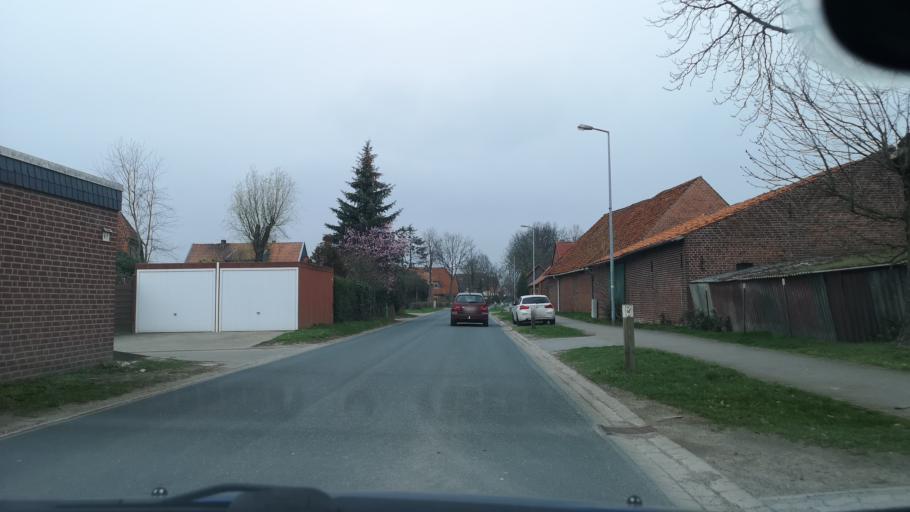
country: DE
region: Lower Saxony
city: Neustadt am Rubenberge
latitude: 52.5062
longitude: 9.5252
